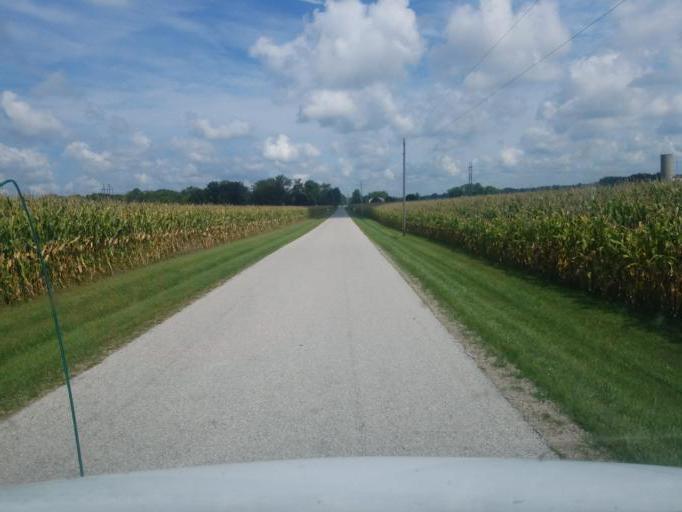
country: US
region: Ohio
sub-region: Marion County
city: Marion
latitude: 40.5066
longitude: -83.0838
